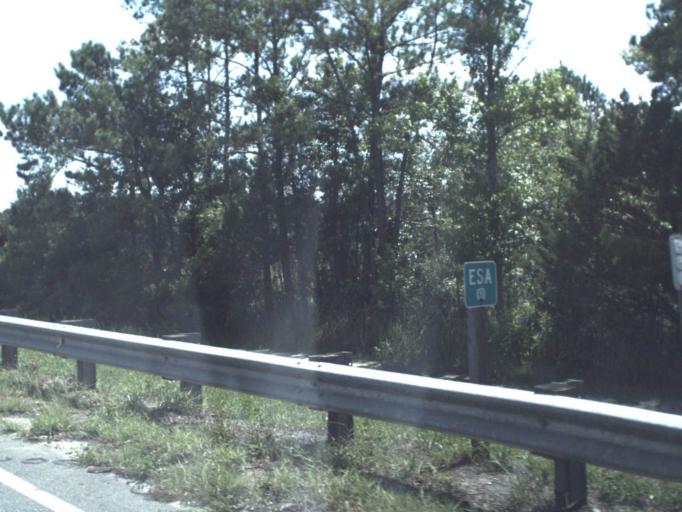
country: US
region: Georgia
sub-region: Camden County
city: Kingsland
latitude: 30.7426
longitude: -81.6880
